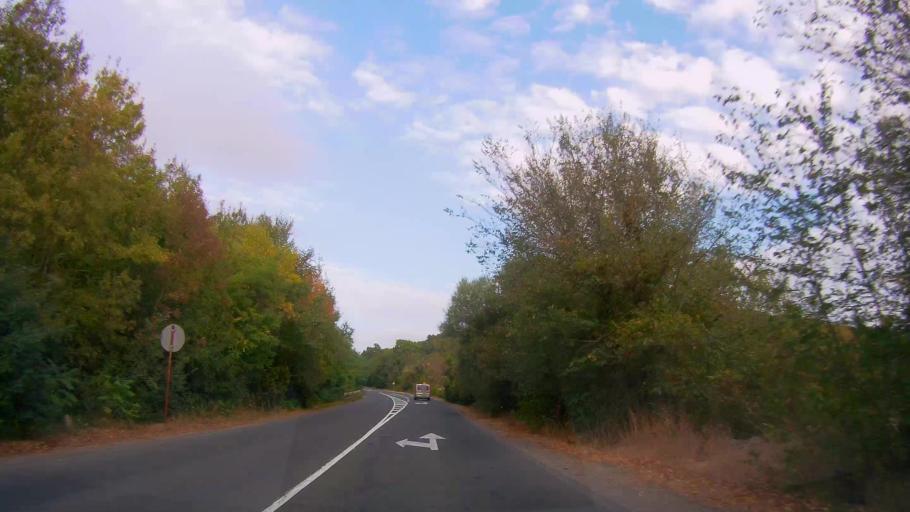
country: BG
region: Burgas
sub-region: Obshtina Primorsko
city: Primorsko
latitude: 42.3324
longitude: 27.7272
